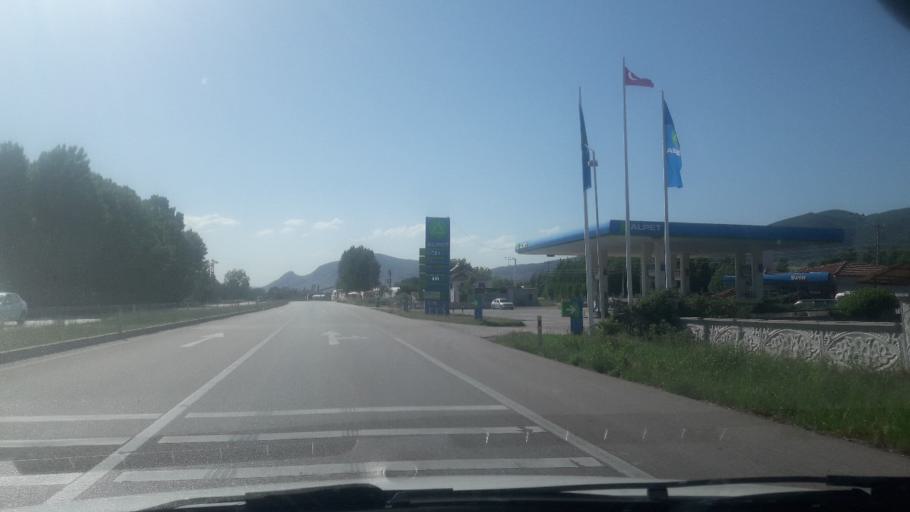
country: TR
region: Tokat
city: Dokmetepe
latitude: 40.3117
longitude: 36.2846
